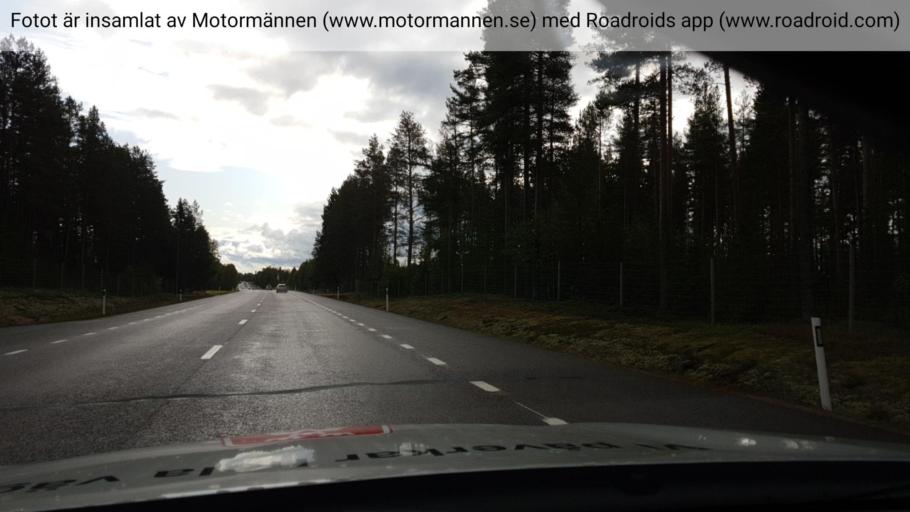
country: SE
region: Norrbotten
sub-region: Bodens Kommun
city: Saevast
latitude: 65.7496
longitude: 21.7664
